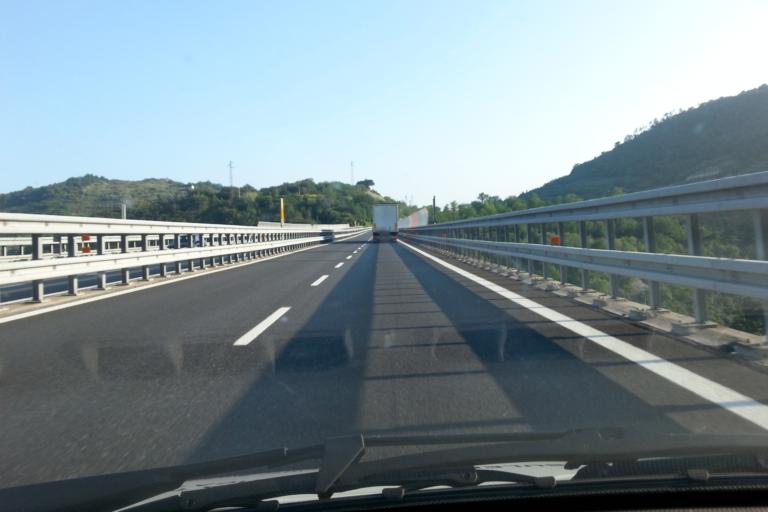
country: IT
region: Liguria
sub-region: Provincia di Savona
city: Tovo San Giacomo
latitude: 44.1629
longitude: 8.2749
